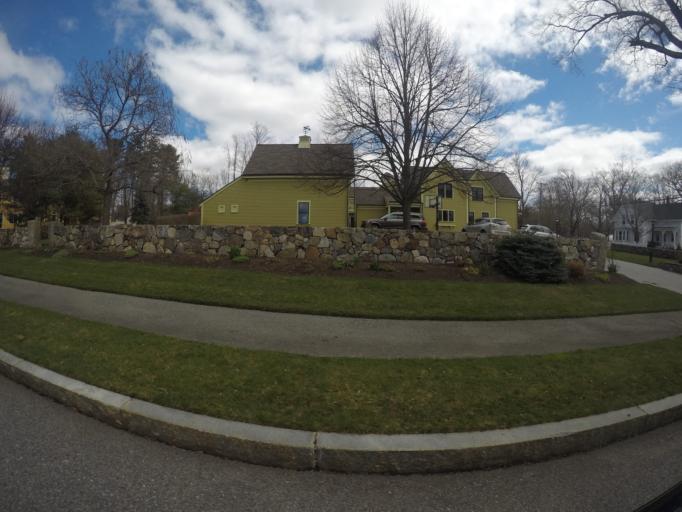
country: US
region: Massachusetts
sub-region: Norfolk County
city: Stoughton
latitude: 42.0750
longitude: -71.0900
